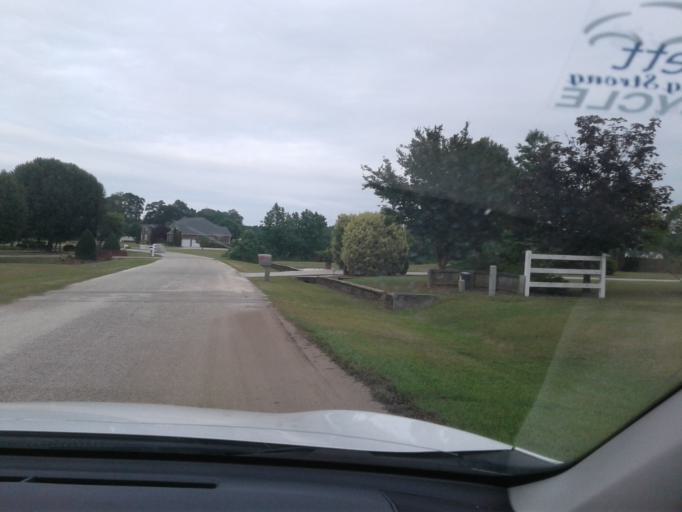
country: US
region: North Carolina
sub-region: Harnett County
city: Dunn
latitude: 35.3375
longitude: -78.5819
